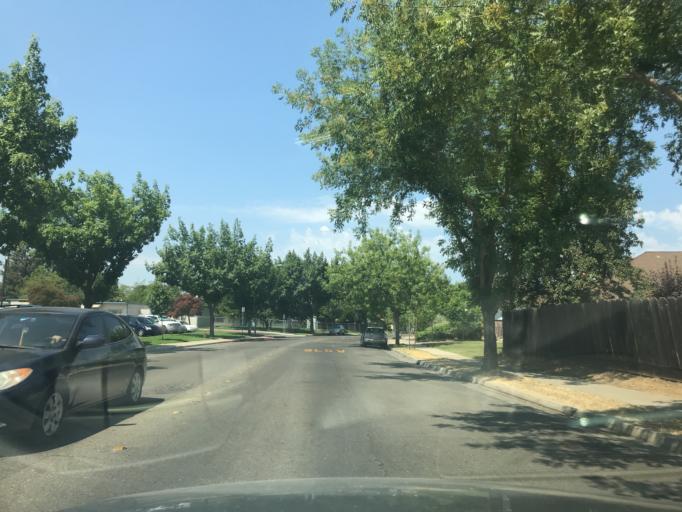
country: US
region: California
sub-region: Merced County
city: Merced
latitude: 37.3285
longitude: -120.4607
